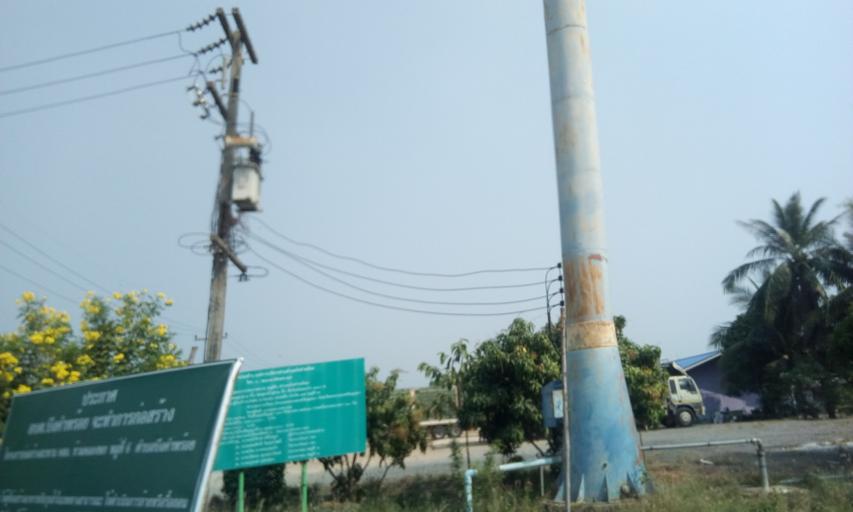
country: TH
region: Pathum Thani
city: Lam Luk Ka
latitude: 13.9489
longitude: 100.7248
